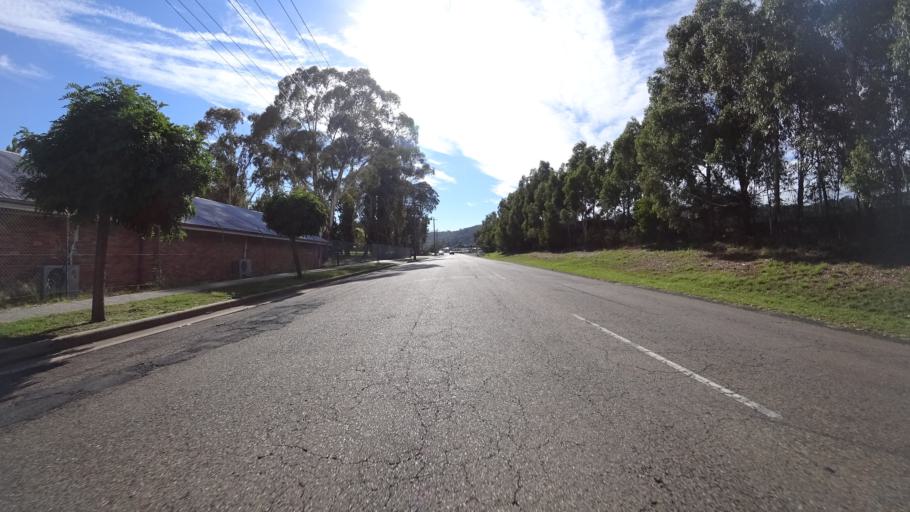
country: AU
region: New South Wales
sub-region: Lithgow
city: Lithgow
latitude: -33.4783
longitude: 150.1643
